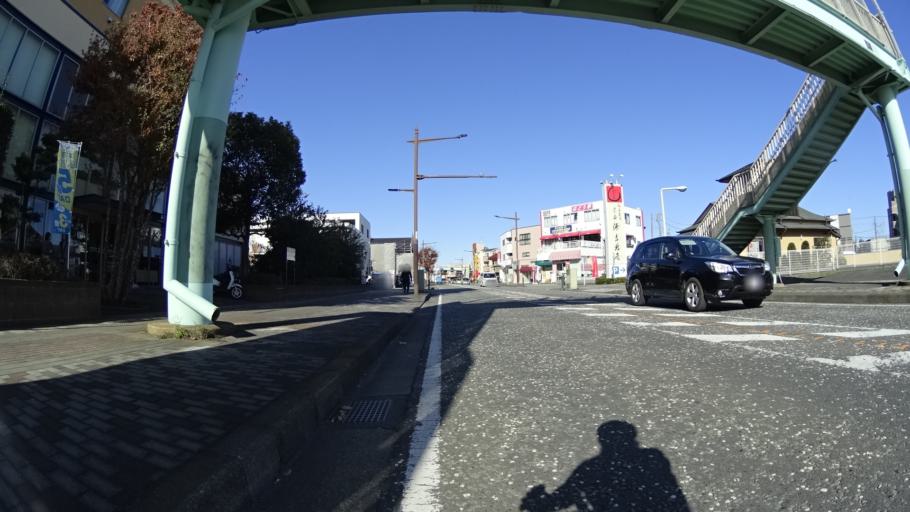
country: JP
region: Kanagawa
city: Zama
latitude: 35.5664
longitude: 139.3608
